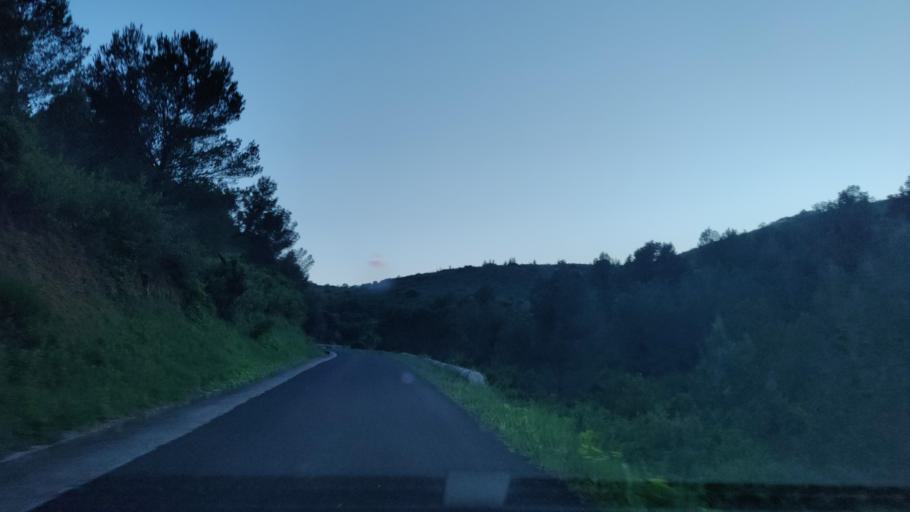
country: FR
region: Languedoc-Roussillon
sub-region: Departement des Pyrenees-Orientales
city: Estagel
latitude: 42.8535
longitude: 2.7691
